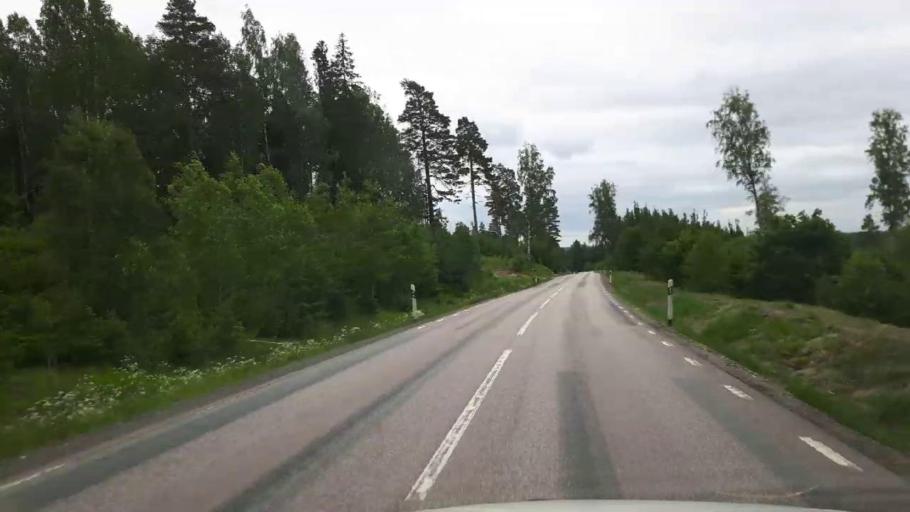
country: SE
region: Vaestmanland
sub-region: Kopings Kommun
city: Kolsva
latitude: 59.6401
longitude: 15.7954
